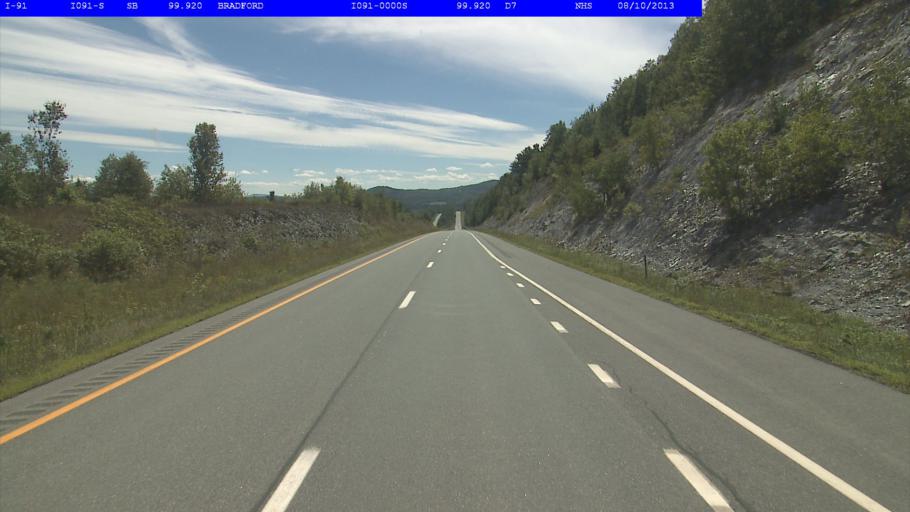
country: US
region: New Hampshire
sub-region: Grafton County
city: Haverhill
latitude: 44.0144
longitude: -72.1224
